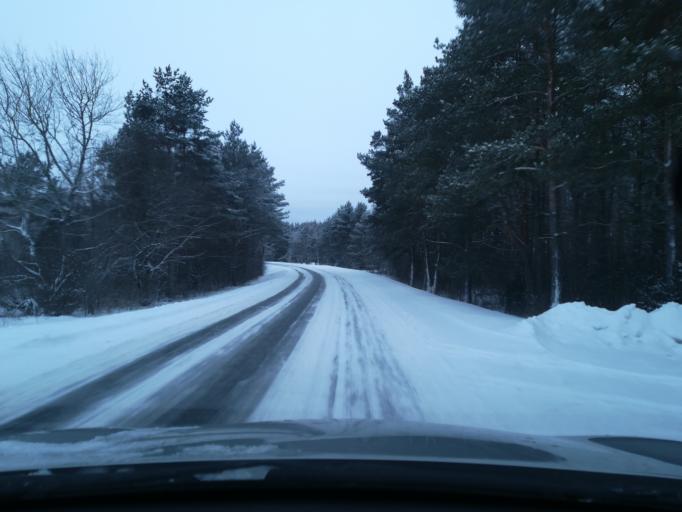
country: EE
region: Harju
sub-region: Keila linn
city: Keila
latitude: 59.3626
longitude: 24.3370
